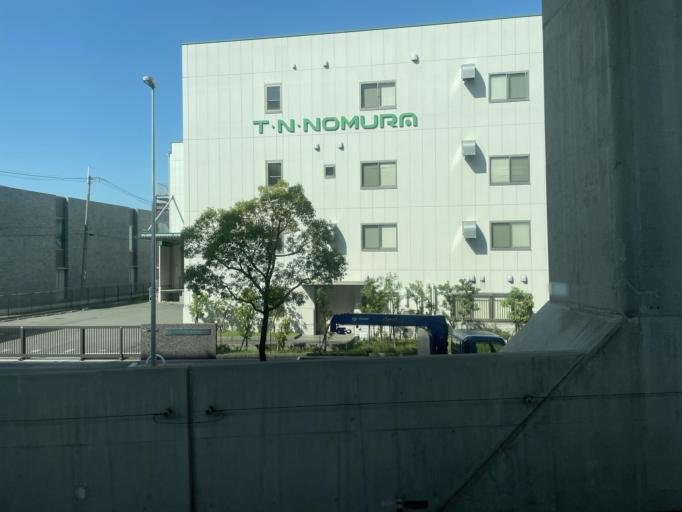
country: JP
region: Osaka
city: Daitocho
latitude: 34.6787
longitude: 135.6133
